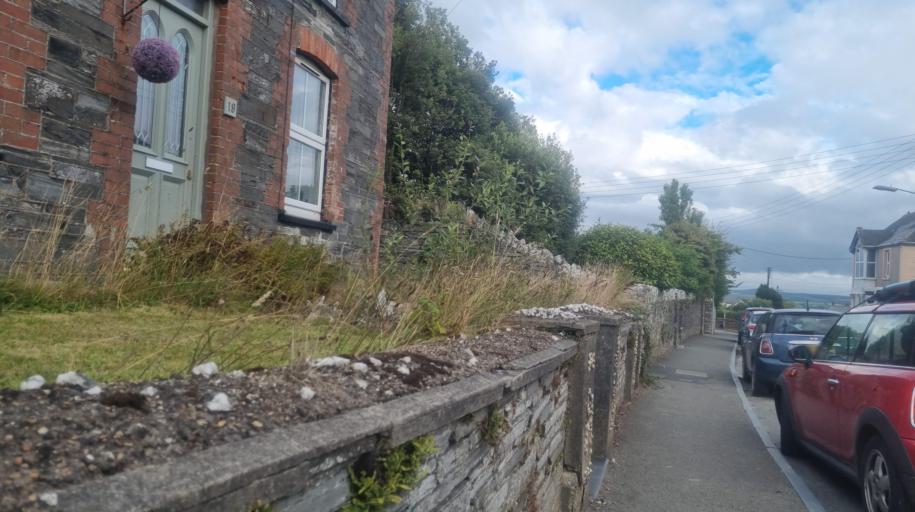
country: GB
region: England
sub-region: Cornwall
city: Tintagel
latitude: 50.6224
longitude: -4.7305
